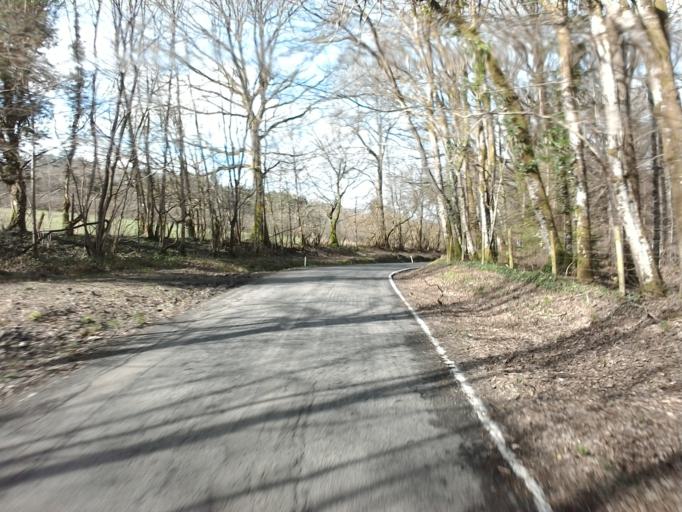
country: BE
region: Wallonia
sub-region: Province du Luxembourg
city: Wellin
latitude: 50.0574
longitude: 5.1384
